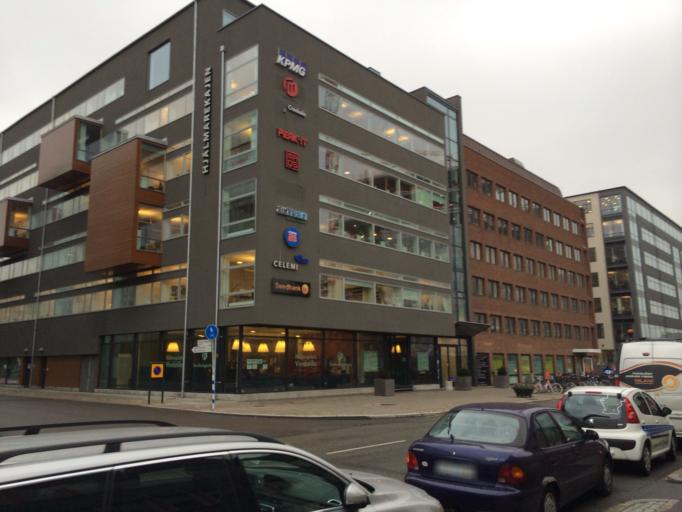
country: SE
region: Skane
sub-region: Malmo
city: Malmoe
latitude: 55.6101
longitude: 12.9948
